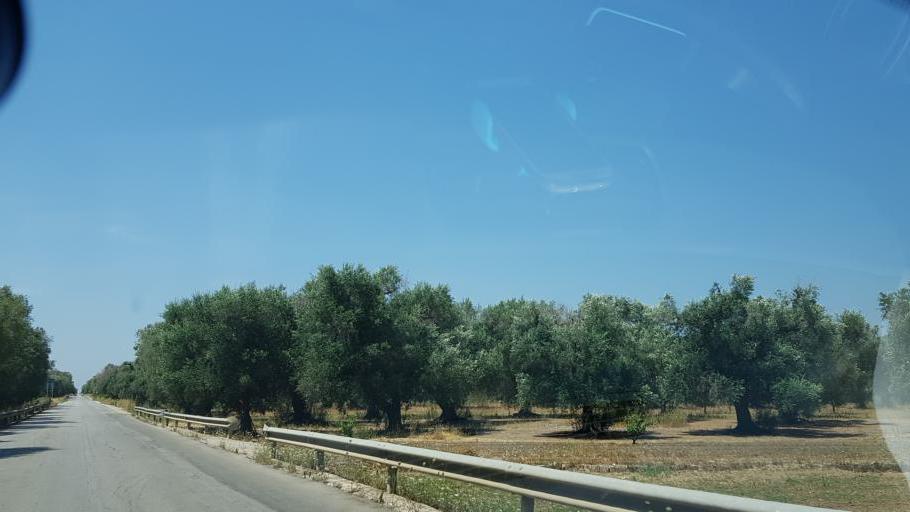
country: IT
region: Apulia
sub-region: Provincia di Brindisi
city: San Donaci
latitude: 40.4680
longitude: 17.9024
